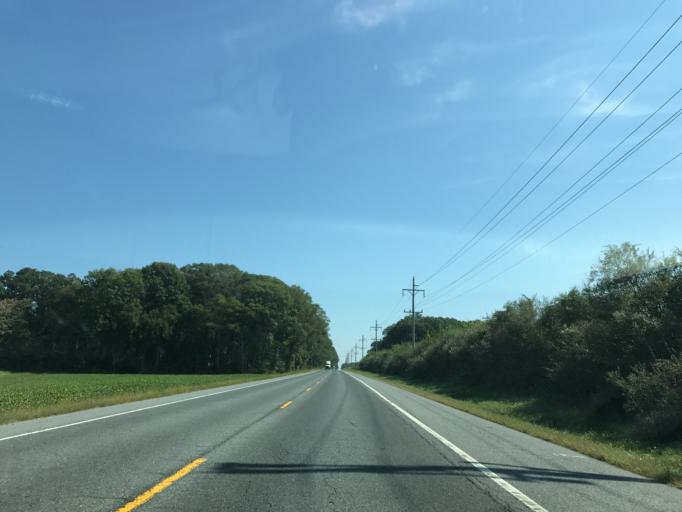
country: US
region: Maryland
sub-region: Queen Anne's County
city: Kingstown
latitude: 39.2626
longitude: -75.9094
